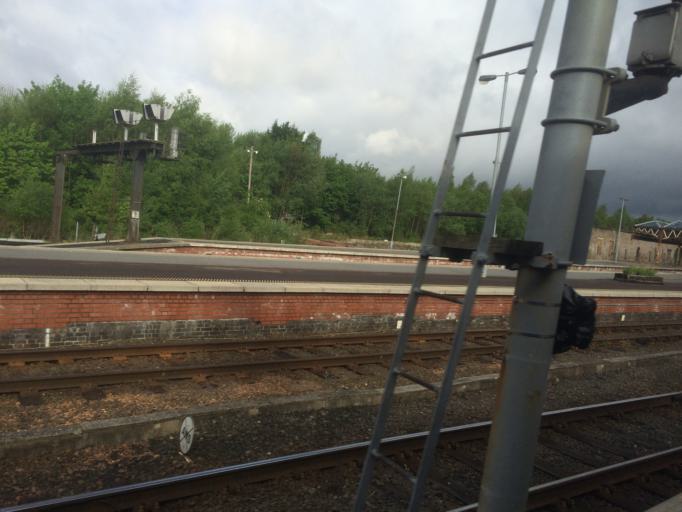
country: GB
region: Scotland
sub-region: Perth and Kinross
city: Perth
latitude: 56.3904
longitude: -3.4382
